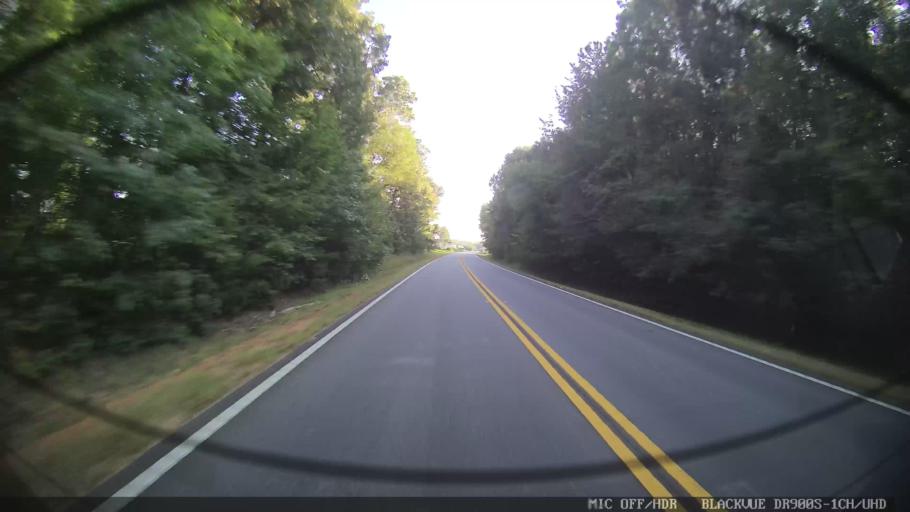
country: US
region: Tennessee
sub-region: Bradley County
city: Wildwood Lake
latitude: 34.9647
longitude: -84.7732
